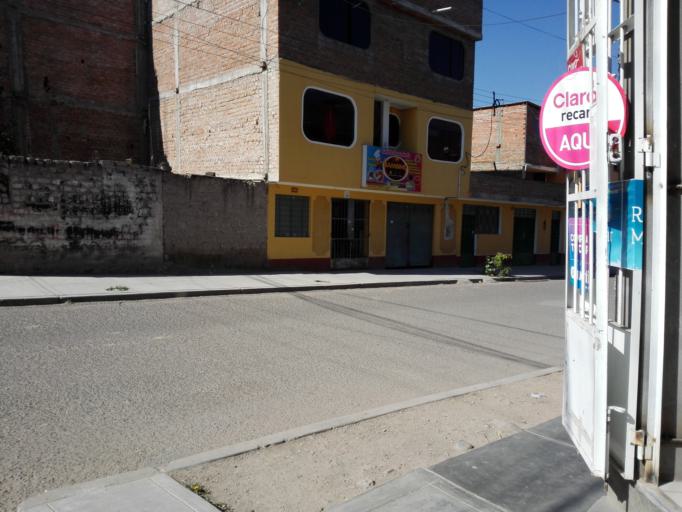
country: PE
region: Ayacucho
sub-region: Provincia de Huamanga
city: Ayacucho
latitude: -13.1516
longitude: -74.2173
